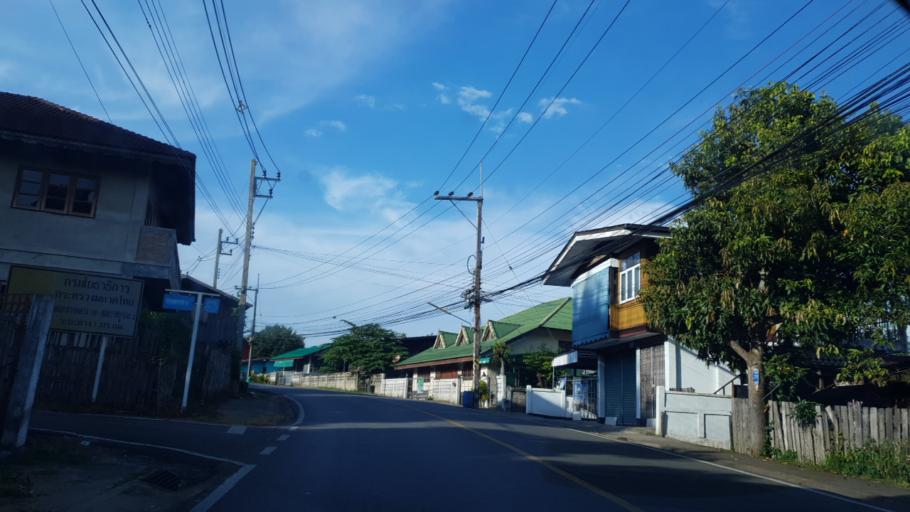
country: TH
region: Mae Hong Son
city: Khun Yuam
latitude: 18.8183
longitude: 97.9375
